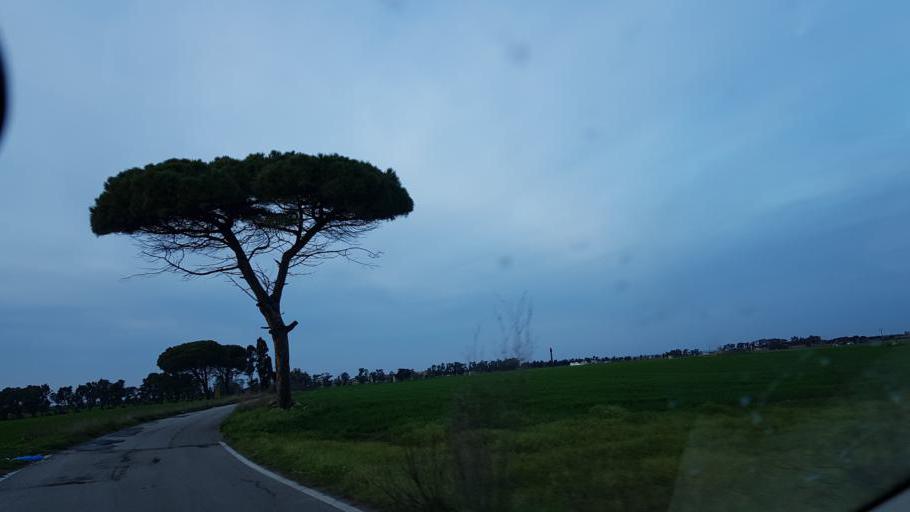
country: IT
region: Apulia
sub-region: Provincia di Brindisi
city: Brindisi
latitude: 40.6672
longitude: 17.9066
